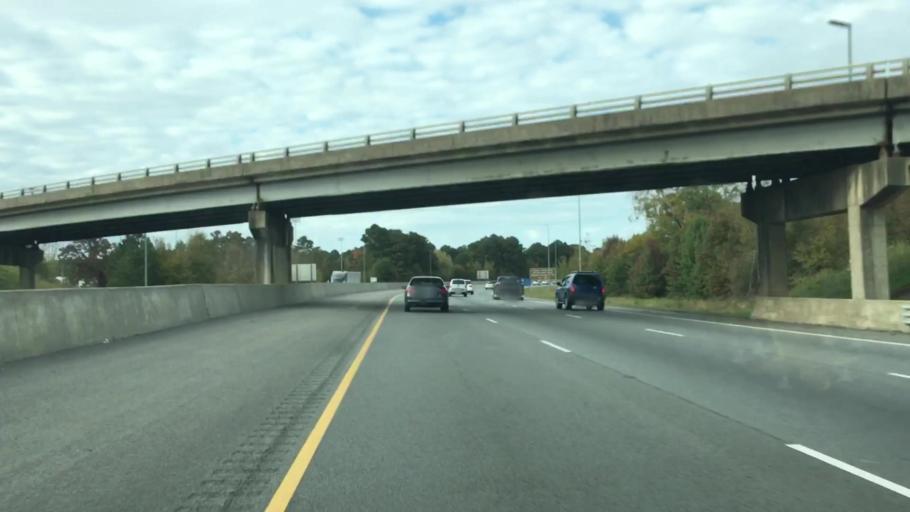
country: US
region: Arkansas
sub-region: Faulkner County
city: Conway
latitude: 35.0989
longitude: -92.4300
